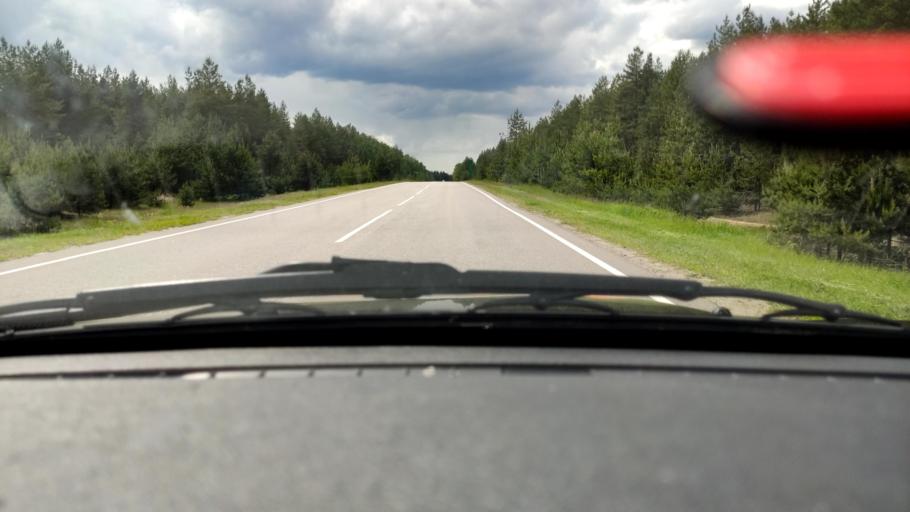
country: RU
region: Voronezj
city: Uryv-Pokrovka
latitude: 51.0543
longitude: 38.9497
